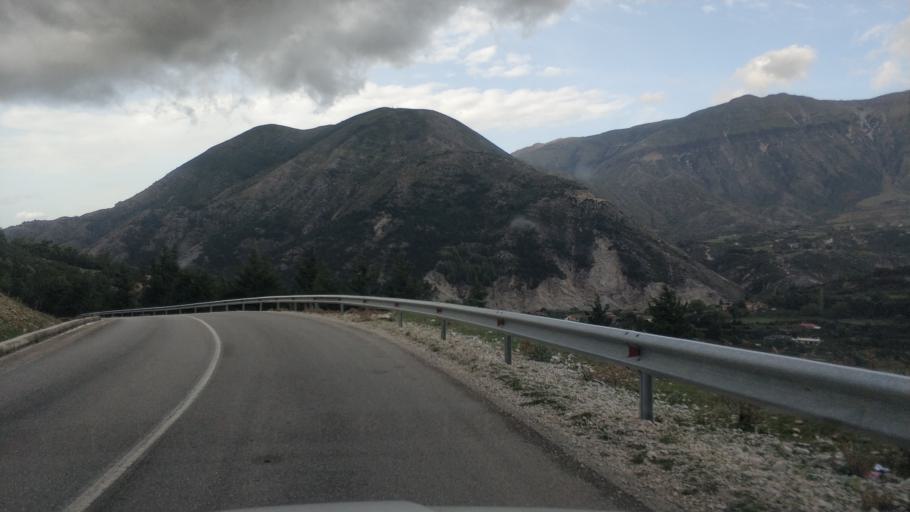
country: AL
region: Vlore
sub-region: Rrethi i Vlores
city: Orikum
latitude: 40.2391
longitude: 19.5517
